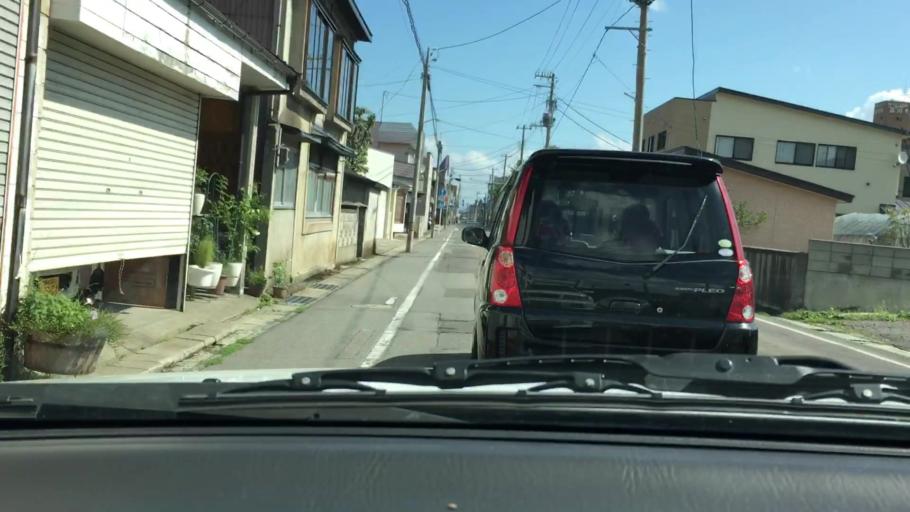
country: JP
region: Aomori
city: Hirosaki
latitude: 40.5950
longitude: 140.4739
